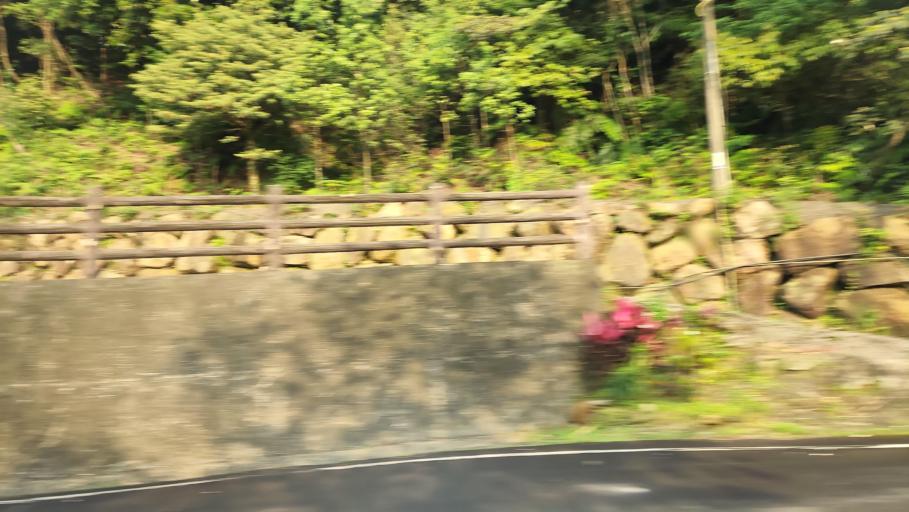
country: TW
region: Taiwan
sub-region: Keelung
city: Keelung
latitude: 25.1538
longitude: 121.6397
